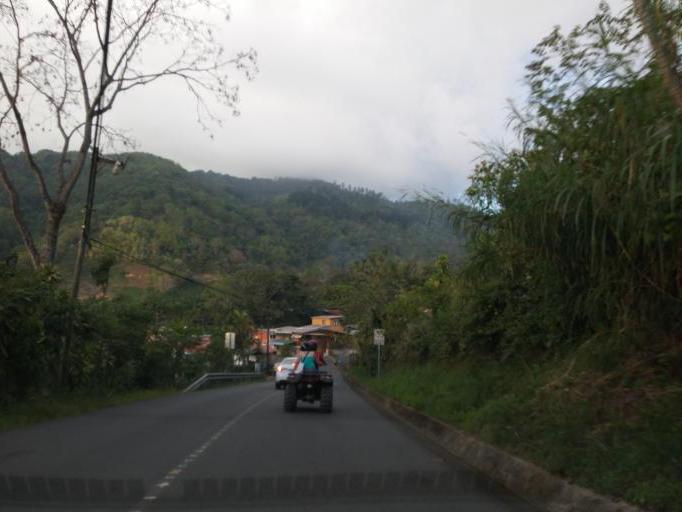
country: CR
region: San Jose
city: Palmichal
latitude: 9.8371
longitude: -84.2056
